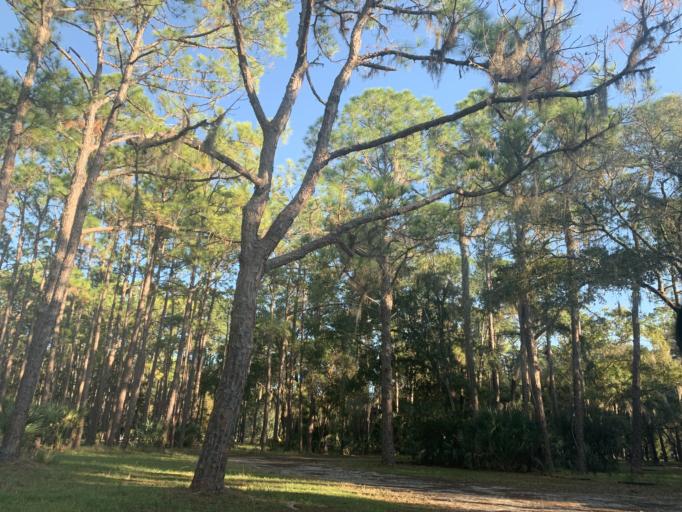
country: US
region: Florida
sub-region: Pinellas County
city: East Lake
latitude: 28.0963
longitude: -82.7099
